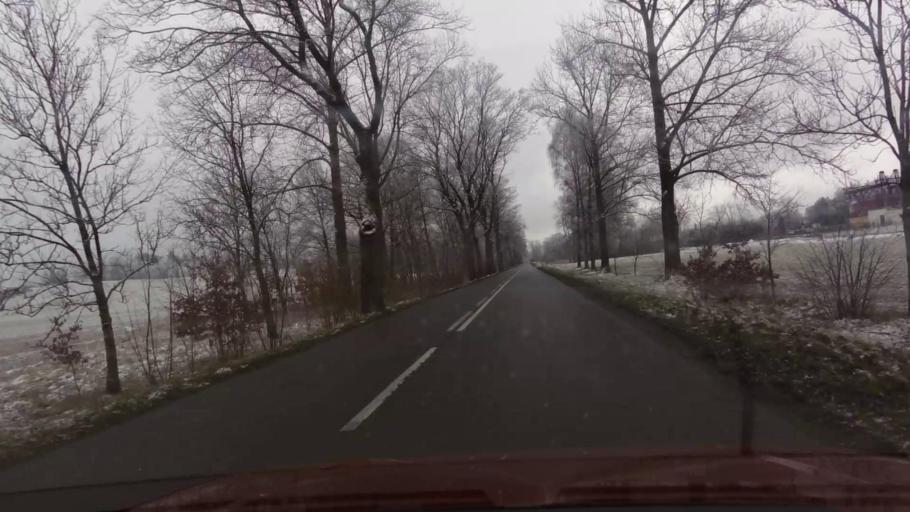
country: PL
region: West Pomeranian Voivodeship
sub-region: Powiat swidwinski
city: Polczyn-Zdroj
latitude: 53.7921
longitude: 16.0335
